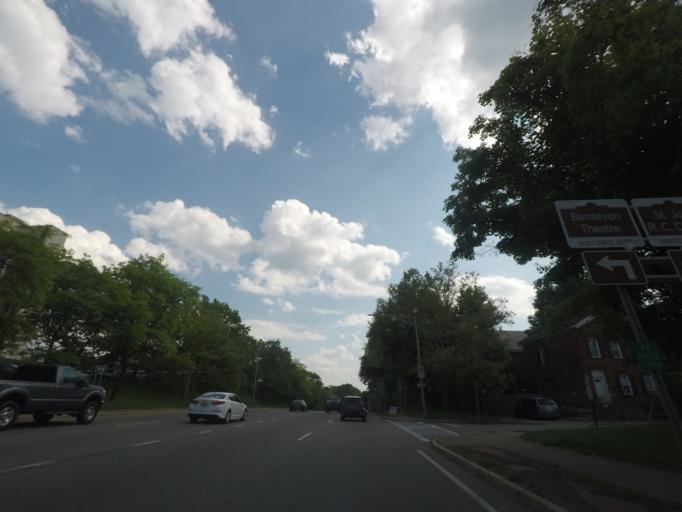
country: US
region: New York
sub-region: Dutchess County
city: Poughkeepsie
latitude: 41.7042
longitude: -73.9304
